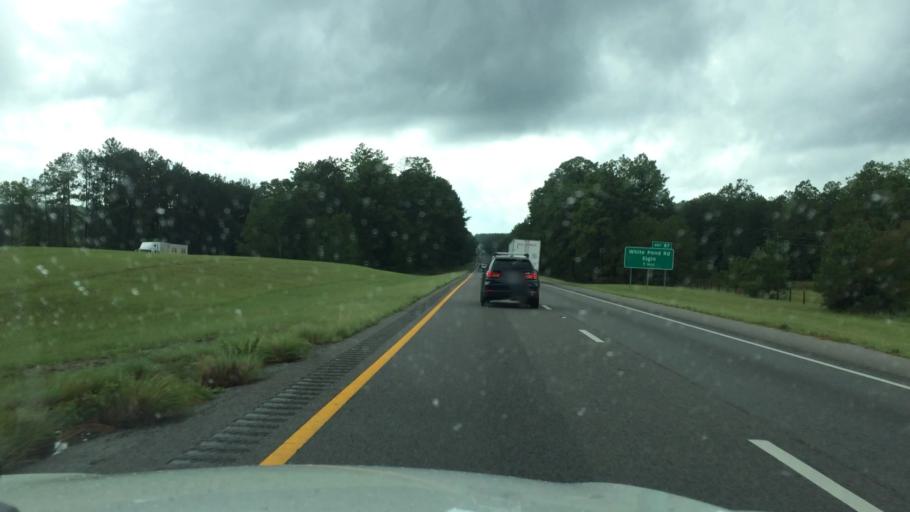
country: US
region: South Carolina
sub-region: Kershaw County
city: Elgin
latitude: 34.1554
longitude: -80.7330
